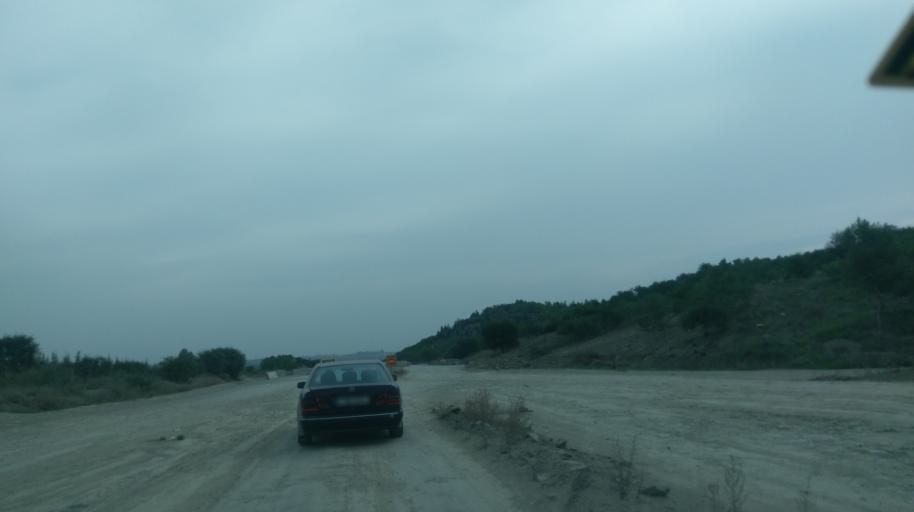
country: CY
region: Lefkosia
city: Nicosia
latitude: 35.2363
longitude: 33.3303
